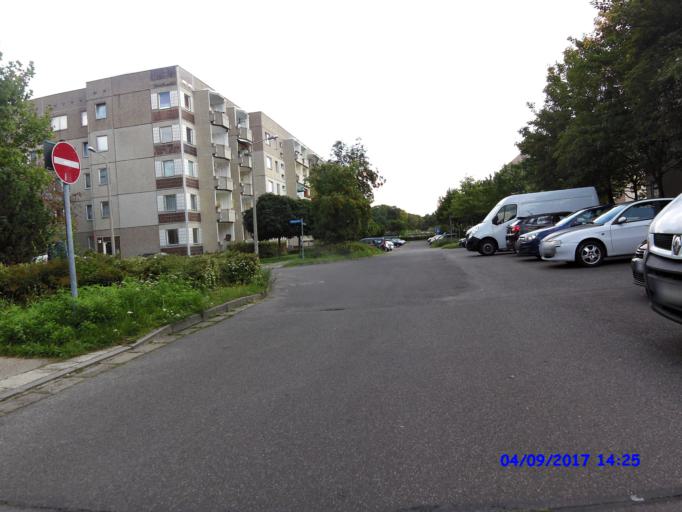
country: DE
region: Saxony
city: Taucha
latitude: 51.3548
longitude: 12.4615
